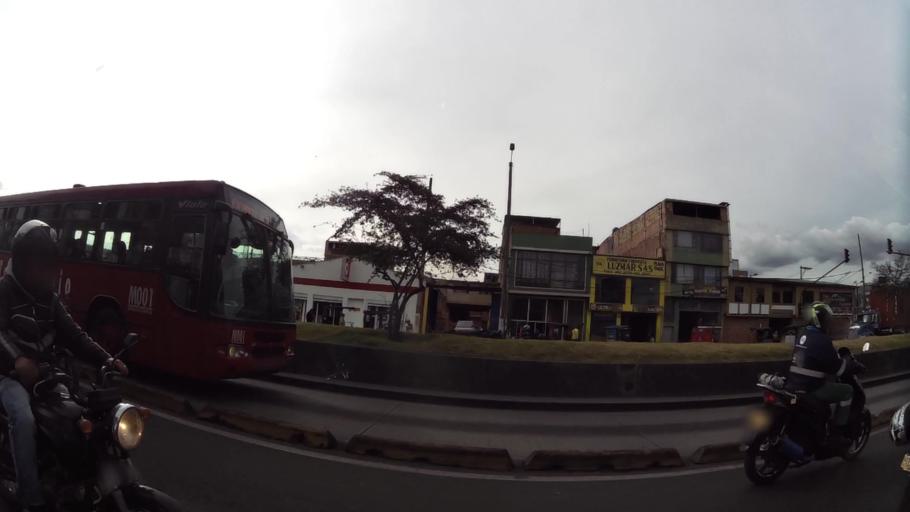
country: CO
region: Cundinamarca
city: Soacha
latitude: 4.6318
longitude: -74.1662
